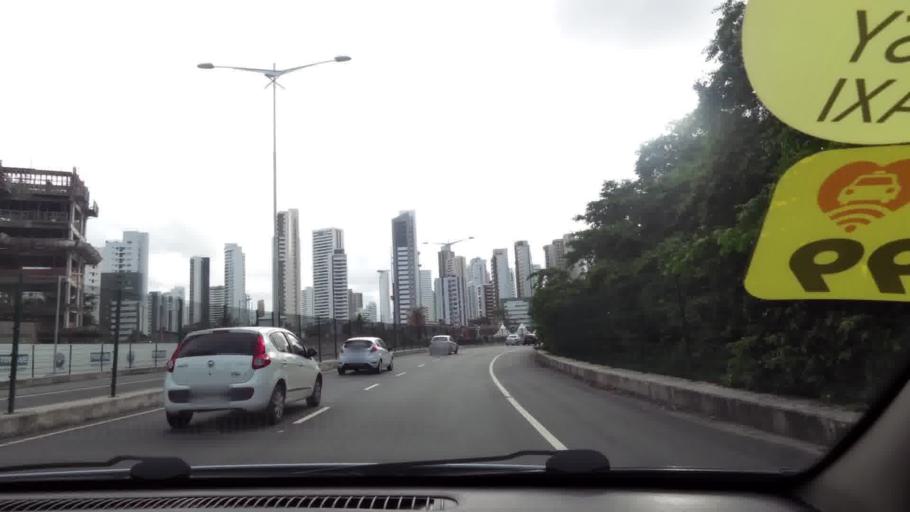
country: BR
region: Pernambuco
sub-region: Recife
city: Recife
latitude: -8.1072
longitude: -34.8941
